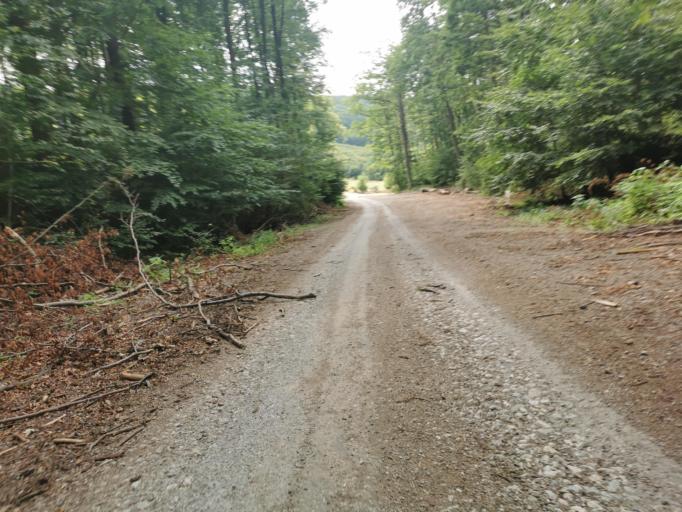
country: SK
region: Trenciansky
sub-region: Okres Myjava
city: Myjava
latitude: 48.7312
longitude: 17.5069
